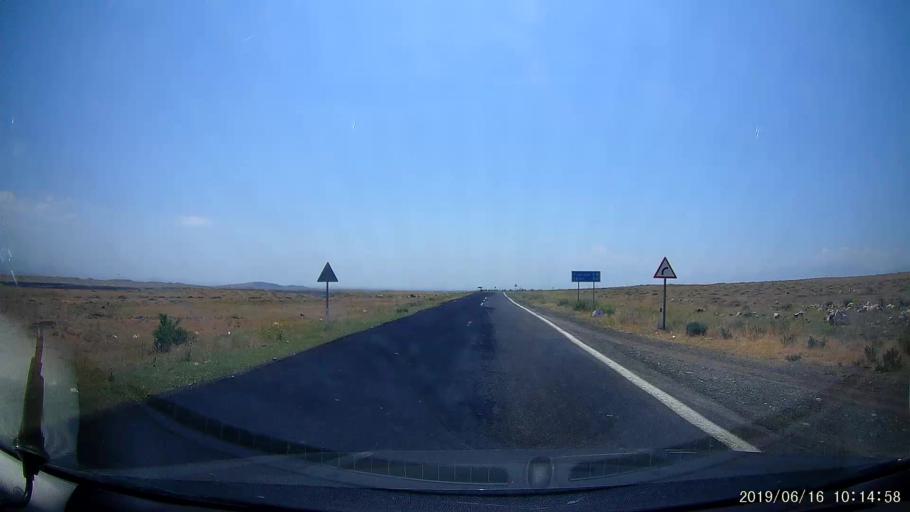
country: TR
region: Igdir
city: Tuzluca
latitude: 40.1802
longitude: 43.6737
